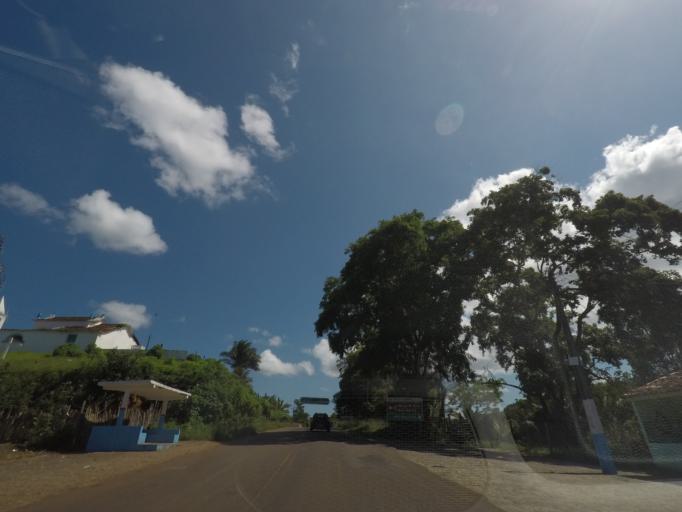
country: BR
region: Bahia
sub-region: Taperoa
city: Taperoa
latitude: -13.5829
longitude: -39.1062
